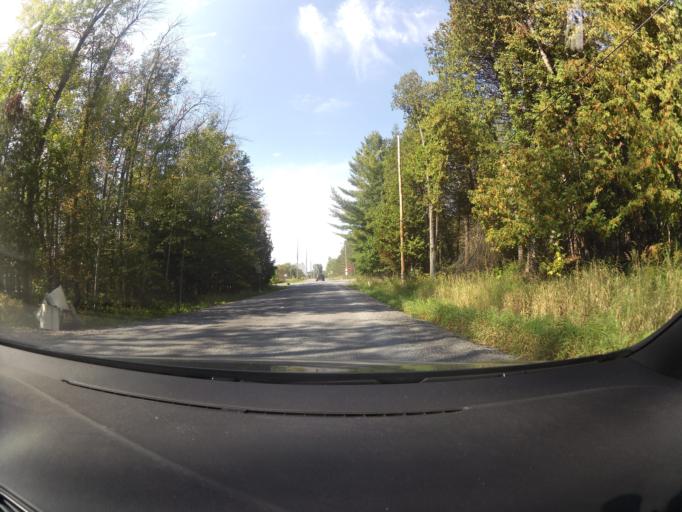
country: CA
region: Ontario
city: Bells Corners
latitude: 45.4586
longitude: -76.0189
